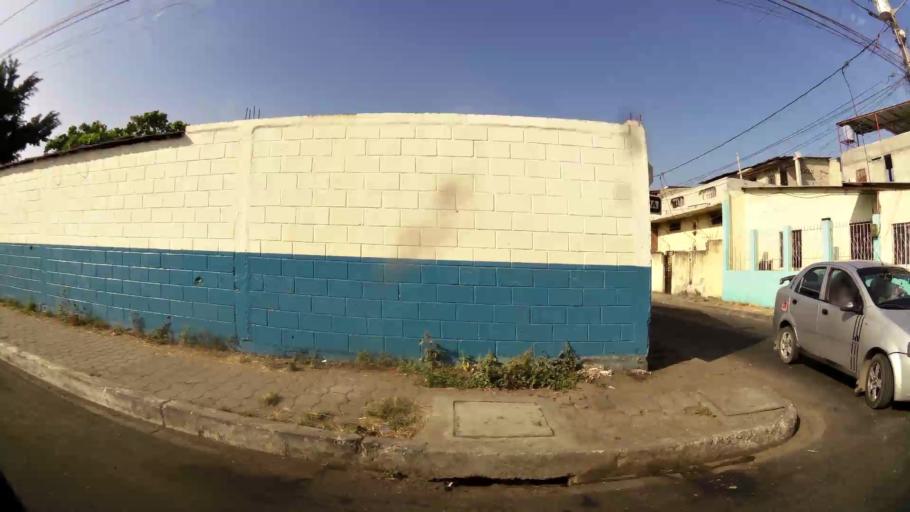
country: EC
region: Guayas
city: Eloy Alfaro
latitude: -2.1704
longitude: -79.8438
